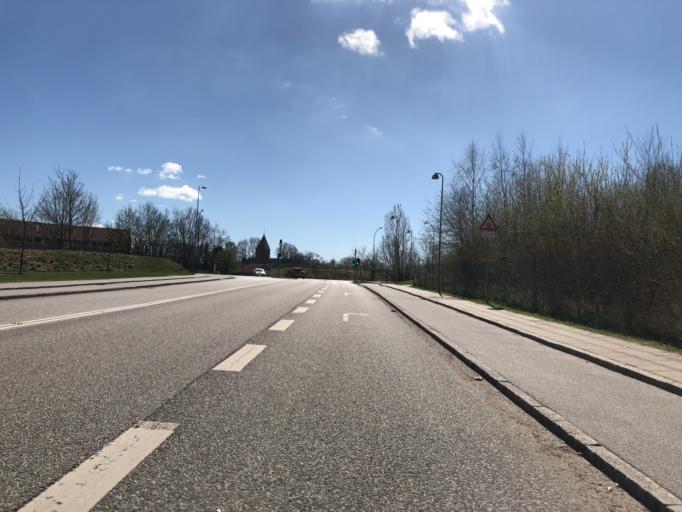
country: DK
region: Zealand
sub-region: Ringsted Kommune
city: Ringsted
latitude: 55.4505
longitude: 11.7836
